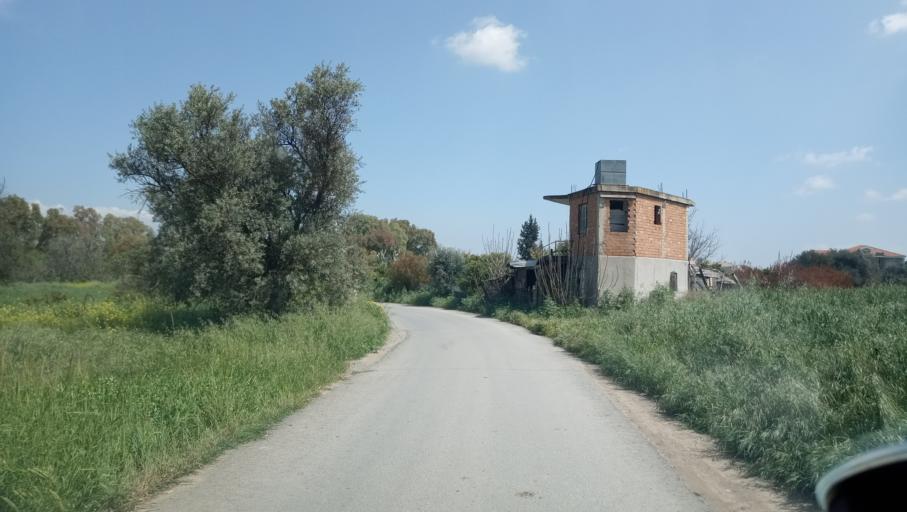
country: CY
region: Lefkosia
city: Dali
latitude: 35.0202
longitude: 33.4056
